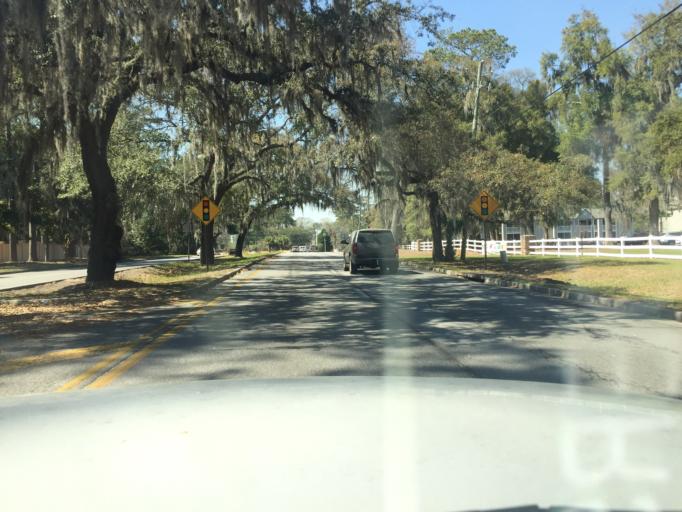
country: US
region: Georgia
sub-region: Chatham County
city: Whitemarsh Island
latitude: 32.0401
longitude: -81.0207
